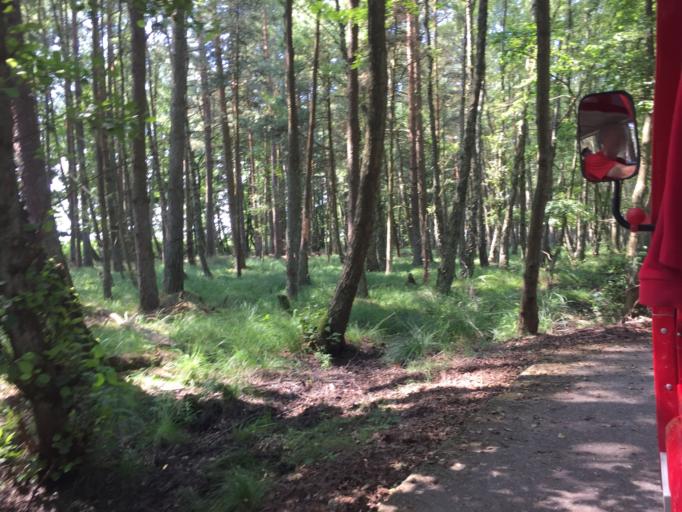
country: PL
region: Pomeranian Voivodeship
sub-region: Powiat leborski
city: Leba
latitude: 54.7526
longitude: 17.4901
